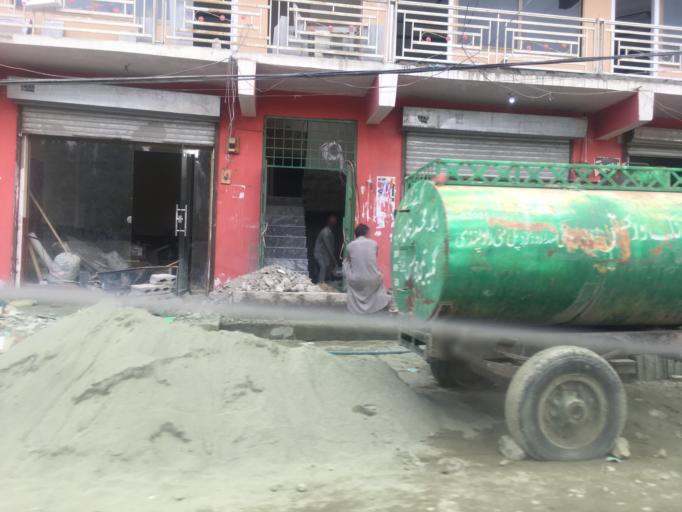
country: PK
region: Gilgit-Baltistan
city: Skardu
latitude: 35.2948
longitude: 75.6082
